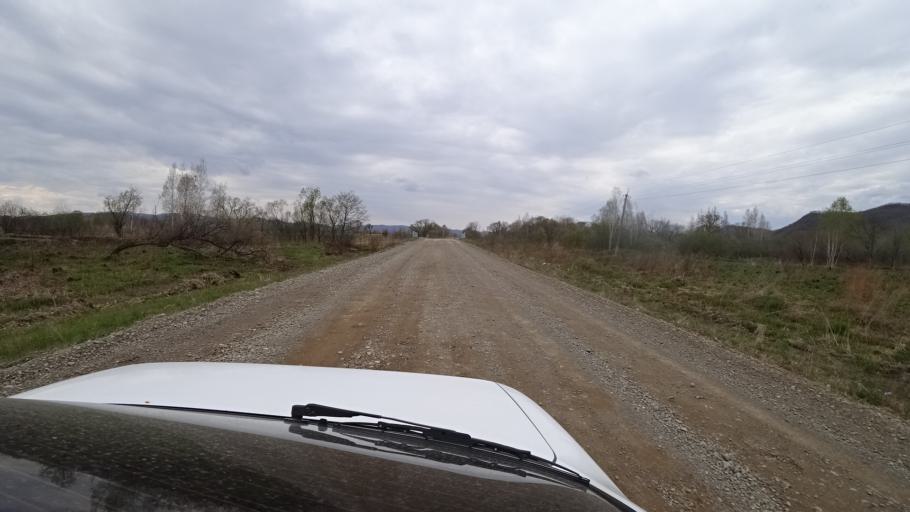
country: RU
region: Primorskiy
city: Novopokrovka
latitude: 45.5620
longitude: 134.3351
